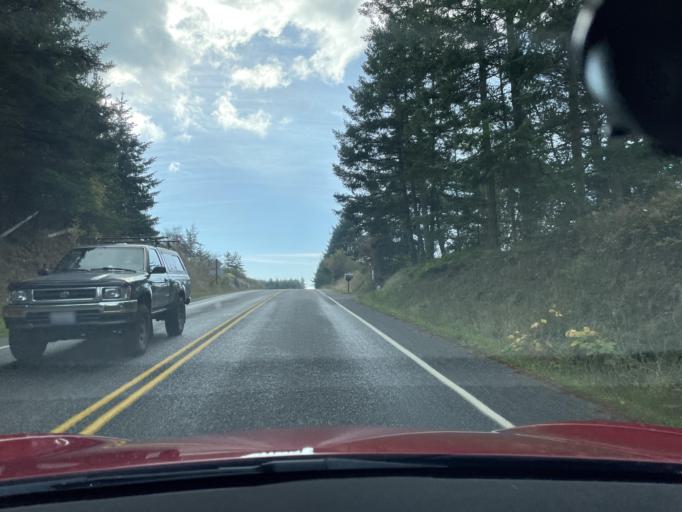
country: US
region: Washington
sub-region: San Juan County
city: Friday Harbor
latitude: 48.4848
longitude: -123.0317
